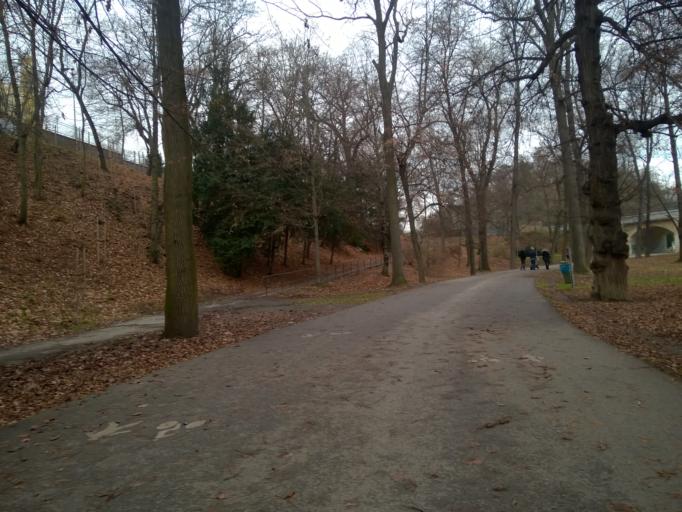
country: CZ
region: Praha
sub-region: Praha 1
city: Mala Strana
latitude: 50.1058
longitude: 14.4070
